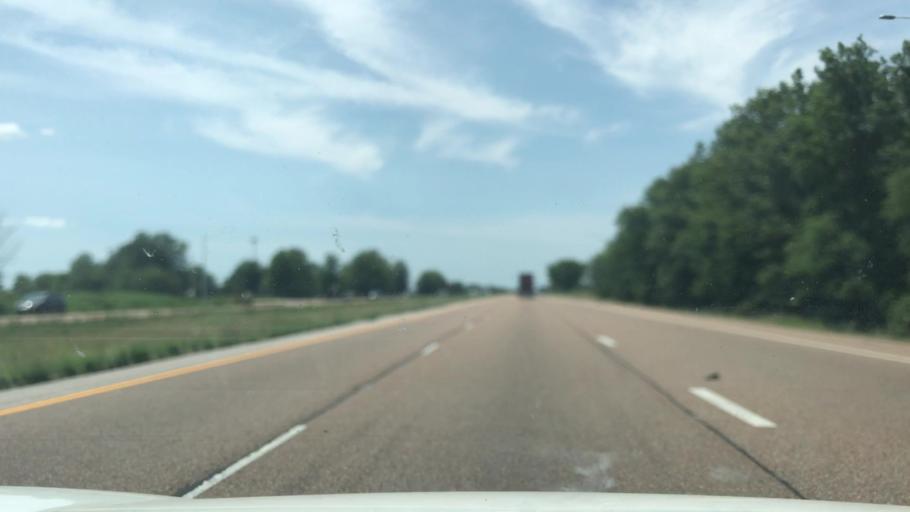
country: US
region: Illinois
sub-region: Saint Clair County
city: Mascoutah
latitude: 38.5489
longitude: -89.7680
